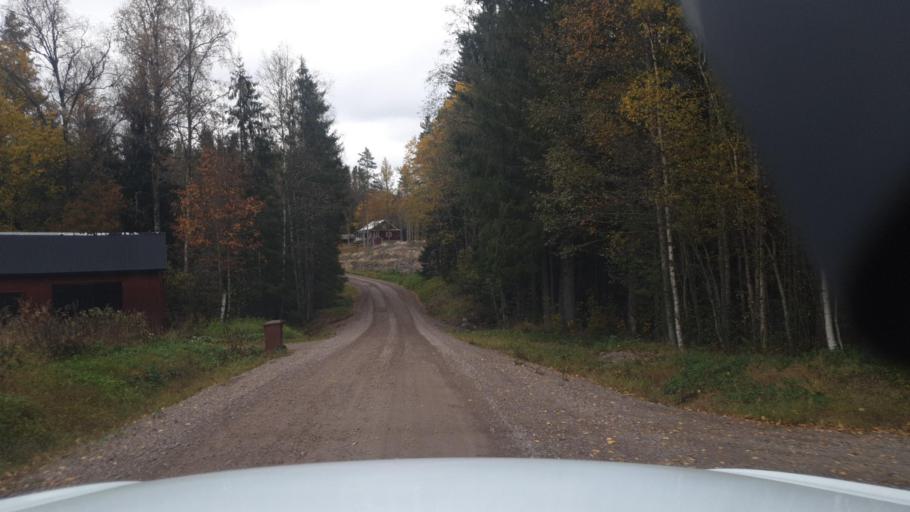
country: SE
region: Vaermland
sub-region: Arvika Kommun
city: Arvika
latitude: 59.9753
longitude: 12.6597
